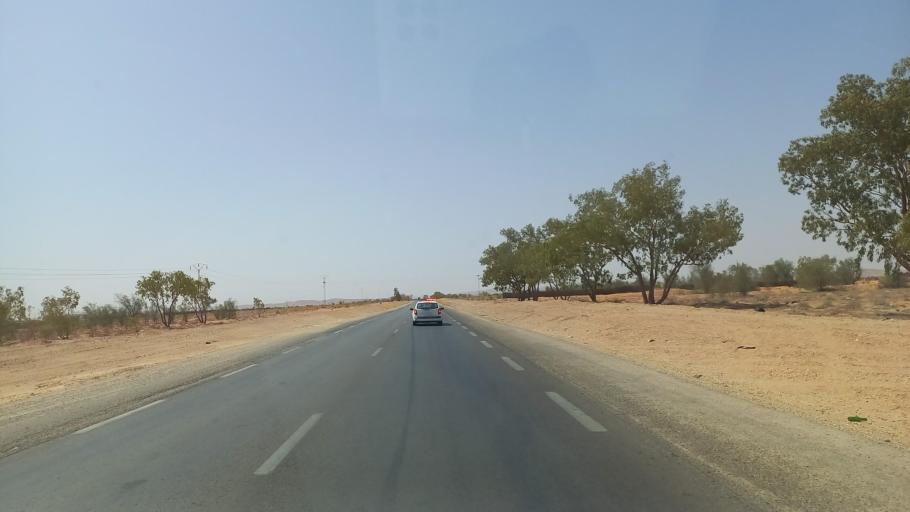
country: TN
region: Madanin
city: Medenine
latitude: 33.2217
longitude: 10.4500
